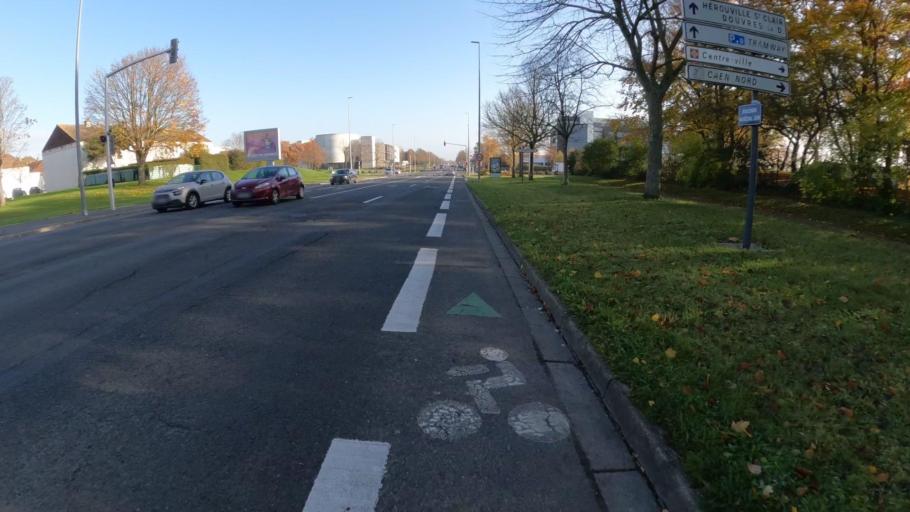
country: FR
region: Lower Normandy
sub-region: Departement du Calvados
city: Epron
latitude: 49.2095
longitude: -0.3722
